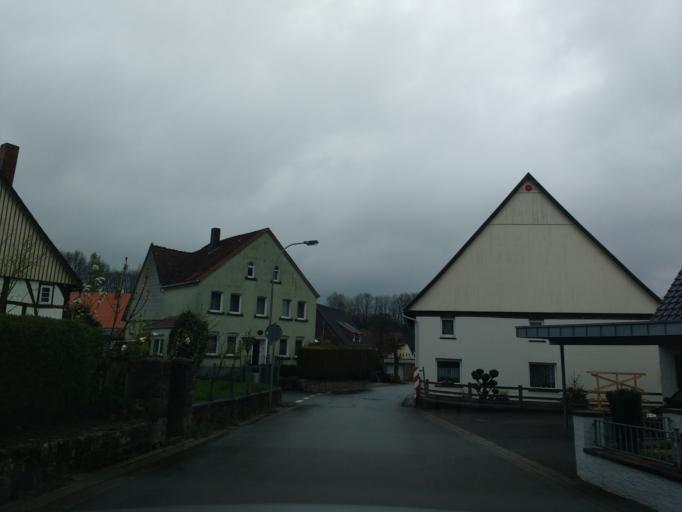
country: DE
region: North Rhine-Westphalia
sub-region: Regierungsbezirk Detmold
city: Bad Meinberg
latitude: 51.9281
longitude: 9.0294
